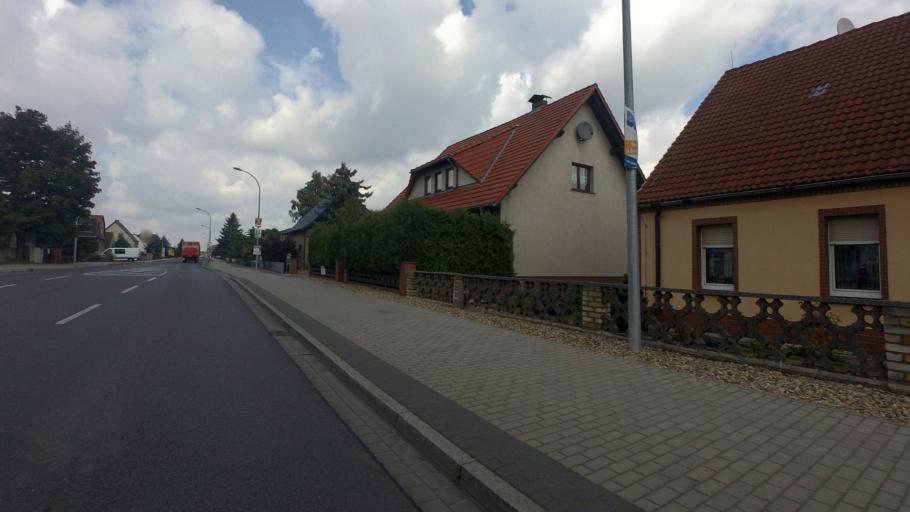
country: DE
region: Brandenburg
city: Herzberg
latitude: 51.6966
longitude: 13.2485
